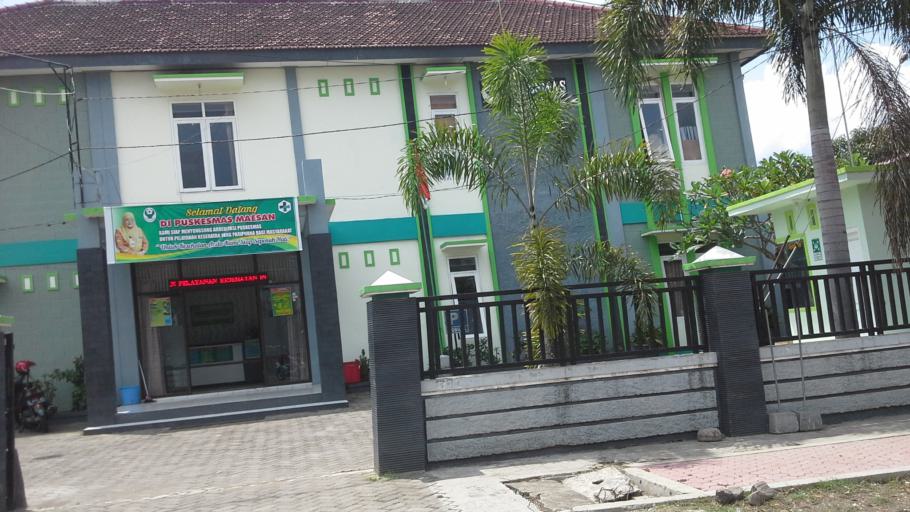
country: ID
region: East Java
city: Krajan Dua Sumbersari
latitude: -8.0325
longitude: 113.7761
